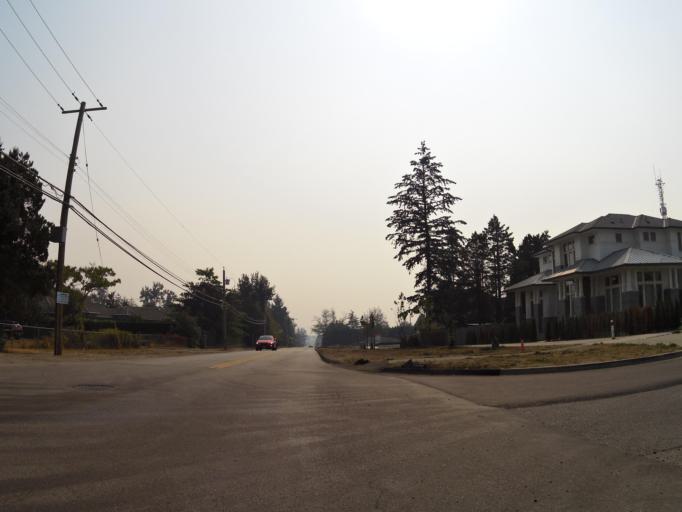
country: US
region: Washington
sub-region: Whatcom County
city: Blaine
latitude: 49.0403
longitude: -122.7572
